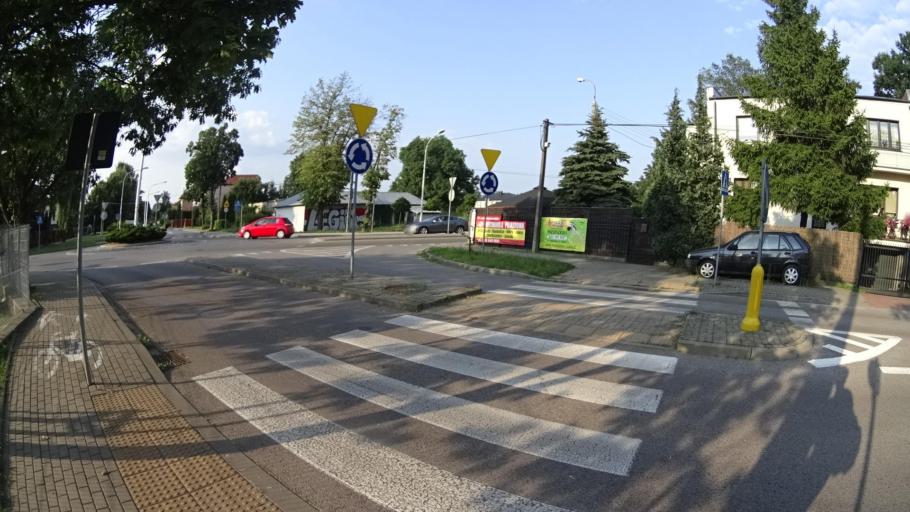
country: PL
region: Masovian Voivodeship
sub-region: Powiat pruszkowski
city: Rybie
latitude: 52.1501
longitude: 20.9306
